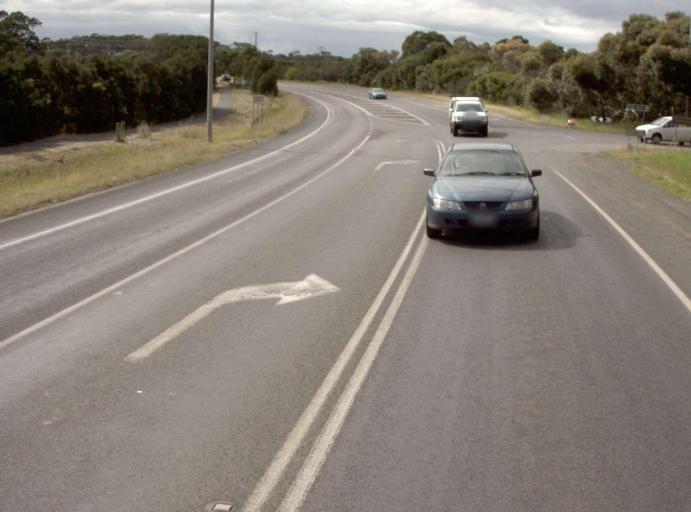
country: AU
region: Victoria
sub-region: Bass Coast
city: Phillip Island
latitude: -38.4807
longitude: 145.2398
